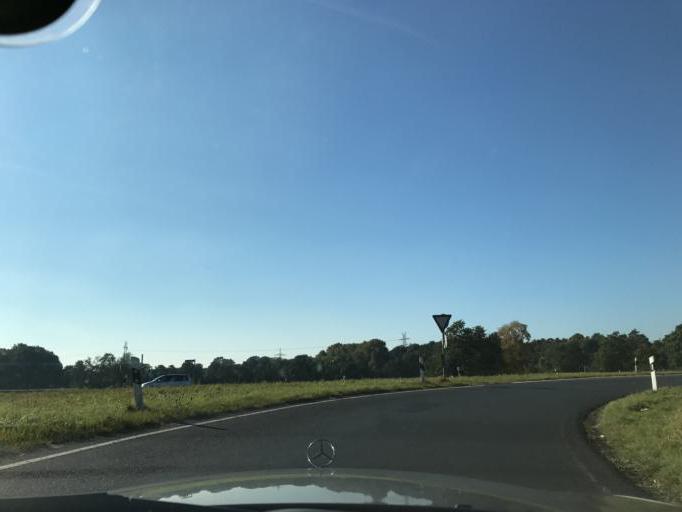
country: DE
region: Lower Saxony
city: Papenburg
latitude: 53.0806
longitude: 7.3793
